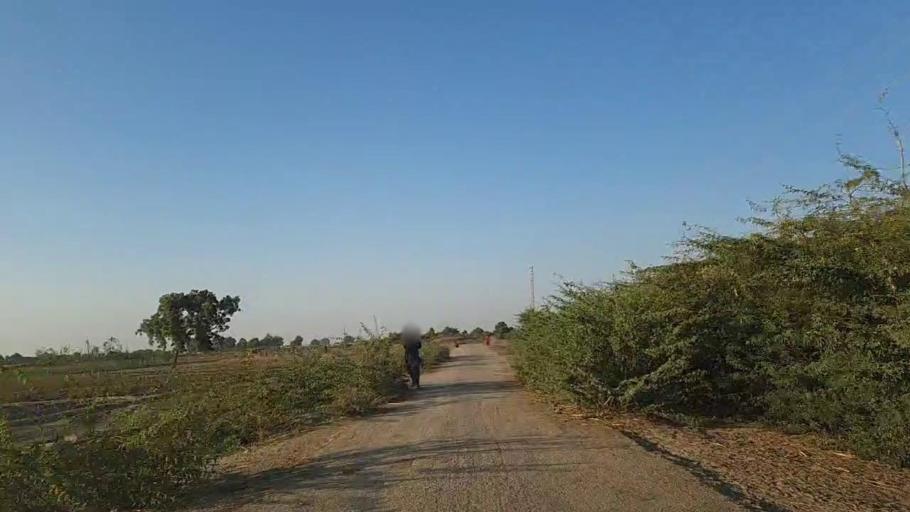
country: PK
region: Sindh
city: Naukot
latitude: 25.0007
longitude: 69.3910
